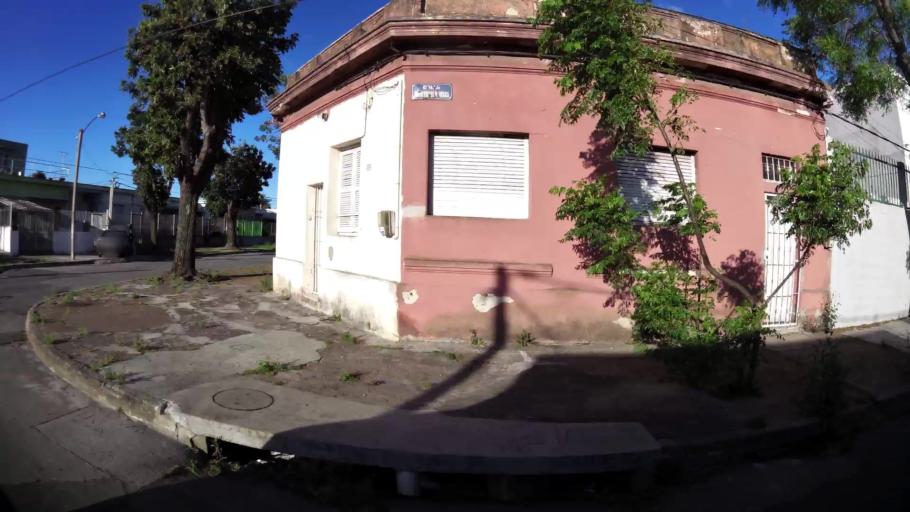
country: UY
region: Montevideo
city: Montevideo
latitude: -34.8677
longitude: -56.1482
